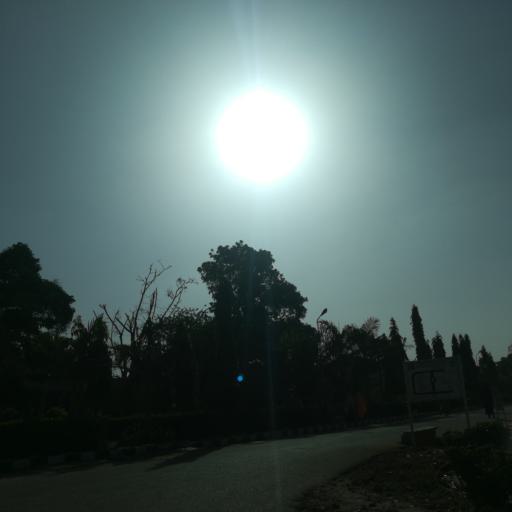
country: NG
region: Kano
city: Kano
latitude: 12.0201
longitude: 8.5031
